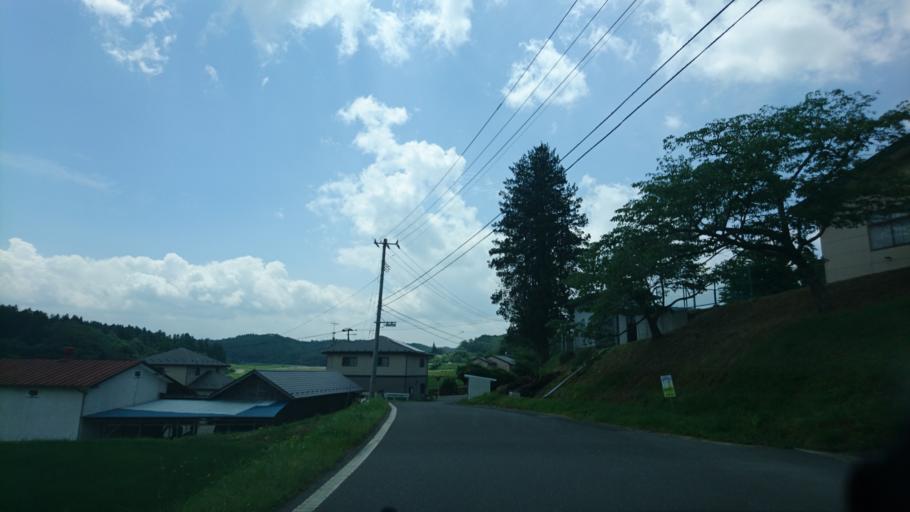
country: JP
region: Iwate
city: Ichinoseki
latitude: 38.9076
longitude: 141.2238
